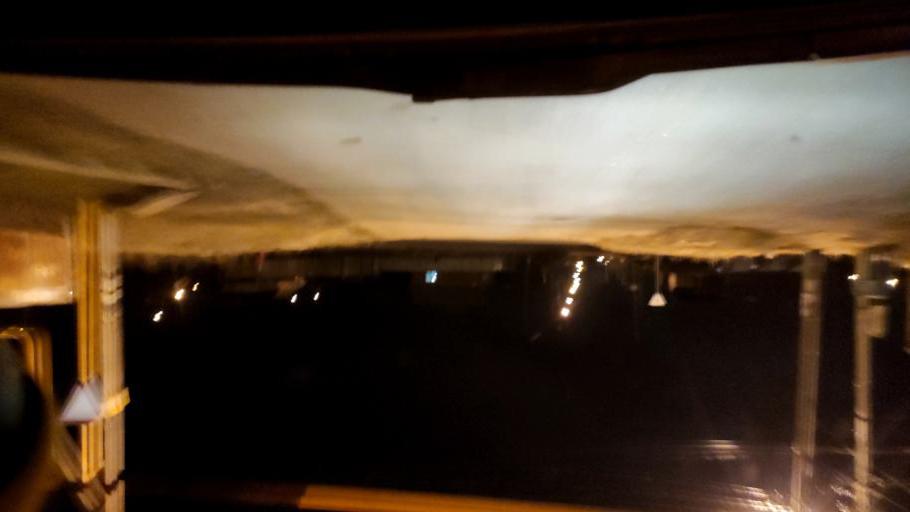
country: RU
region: Samara
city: Zhigulevsk
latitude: 53.4834
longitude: 49.5294
